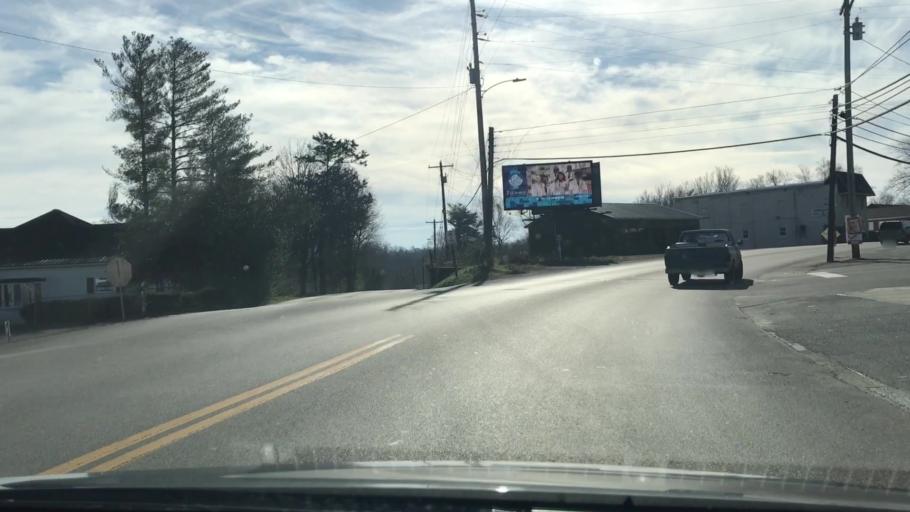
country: US
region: Kentucky
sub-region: Monroe County
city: Tompkinsville
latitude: 36.7047
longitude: -85.6887
